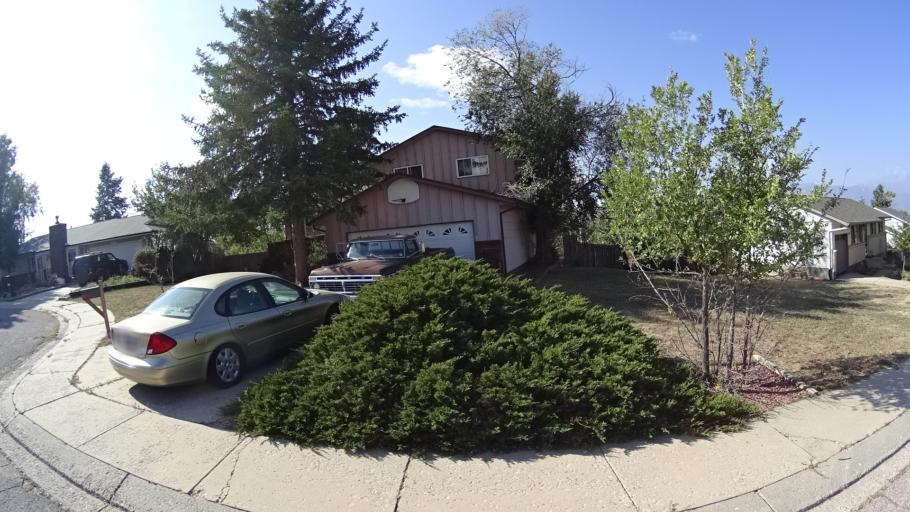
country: US
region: Colorado
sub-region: El Paso County
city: Cimarron Hills
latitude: 38.8820
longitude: -104.7301
